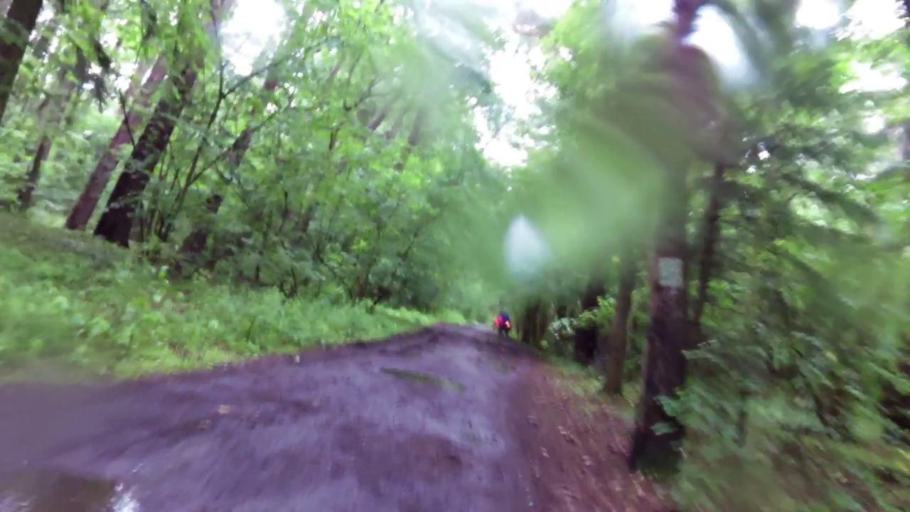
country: PL
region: West Pomeranian Voivodeship
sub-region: Powiat kolobrzeski
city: Ustronie Morskie
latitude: 54.2366
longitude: 15.8397
